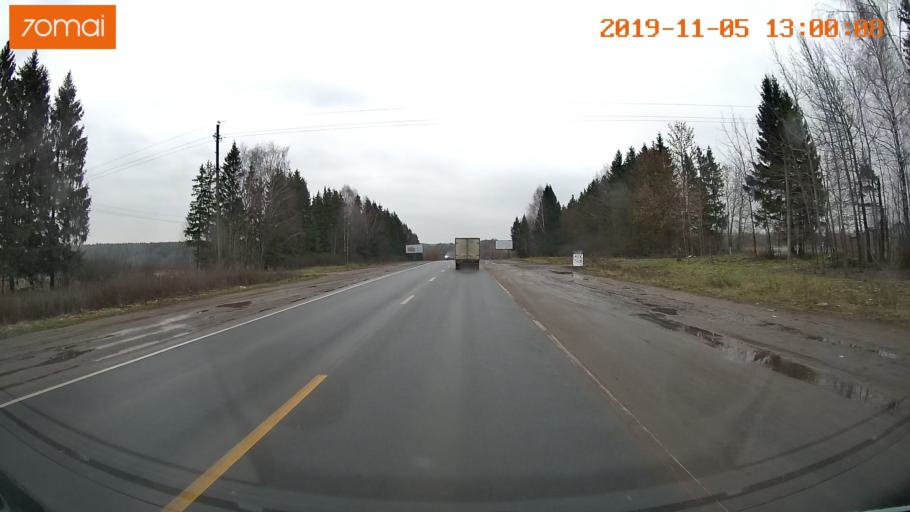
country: RU
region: Ivanovo
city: Kokhma
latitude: 56.9151
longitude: 41.1409
